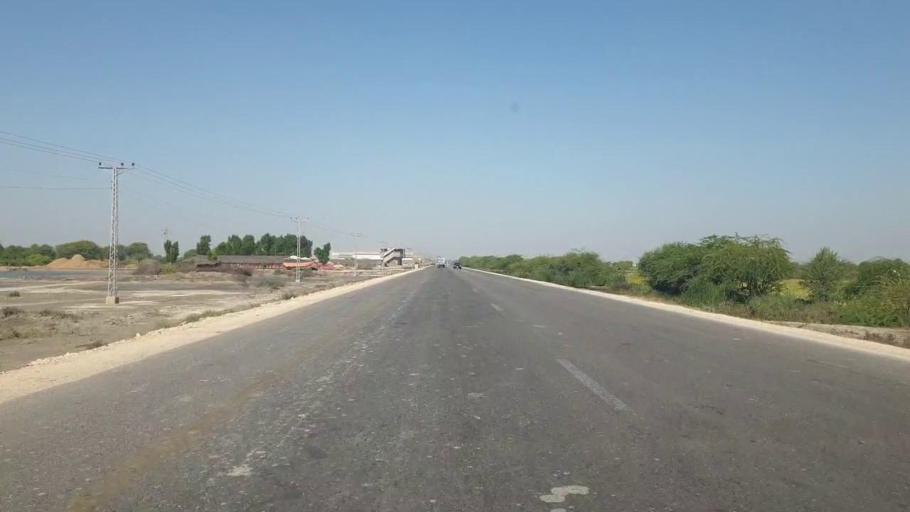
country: PK
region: Sindh
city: Talhar
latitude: 24.8600
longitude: 68.8166
